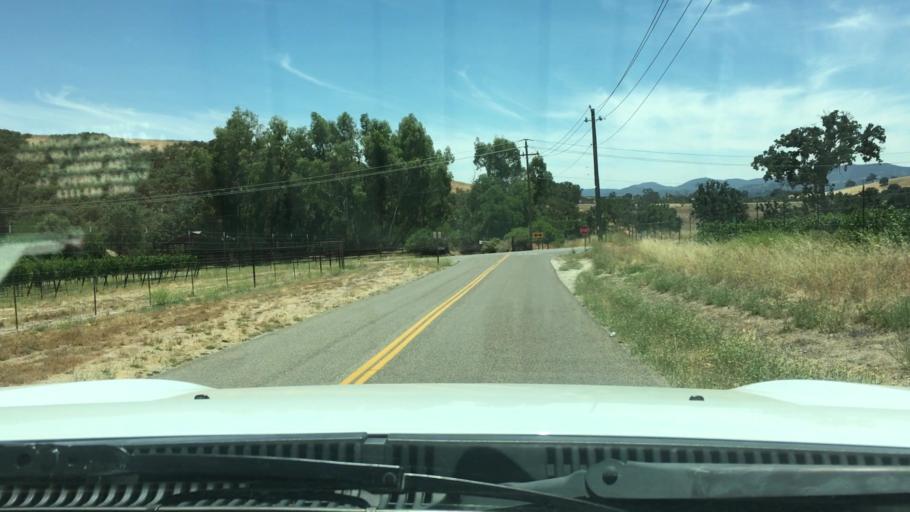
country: US
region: California
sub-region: San Luis Obispo County
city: Templeton
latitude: 35.5627
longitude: -120.6684
